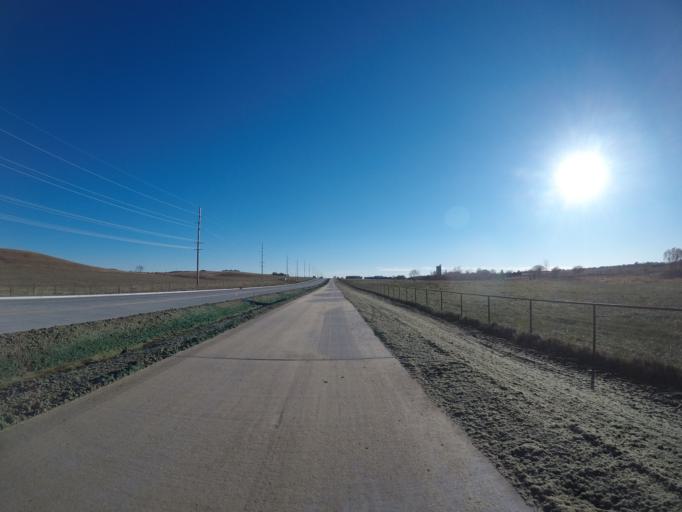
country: US
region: Kansas
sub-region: Riley County
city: Manhattan
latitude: 39.2155
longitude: -96.5858
